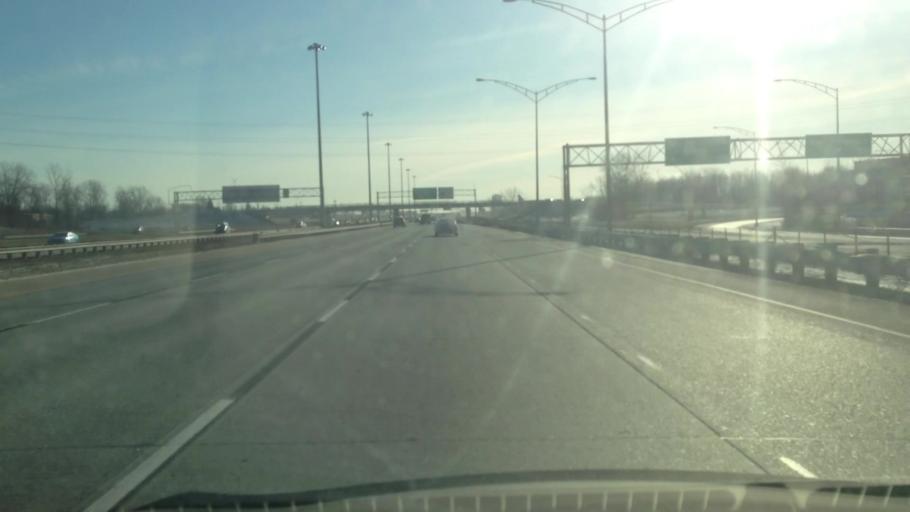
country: CA
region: Quebec
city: Dollard-Des Ormeaux
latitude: 45.5445
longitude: -73.7986
